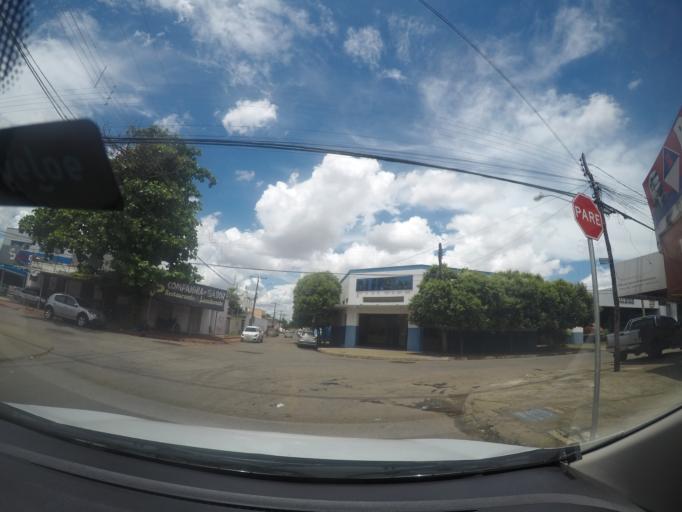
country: BR
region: Goias
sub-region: Goiania
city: Goiania
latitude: -16.6731
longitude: -49.3084
